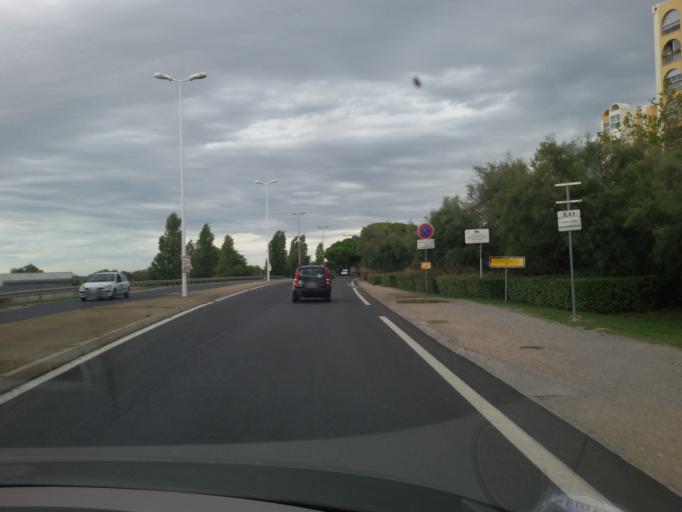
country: FR
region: Languedoc-Roussillon
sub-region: Departement de l'Herault
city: Perols
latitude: 43.5467
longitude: 3.9716
